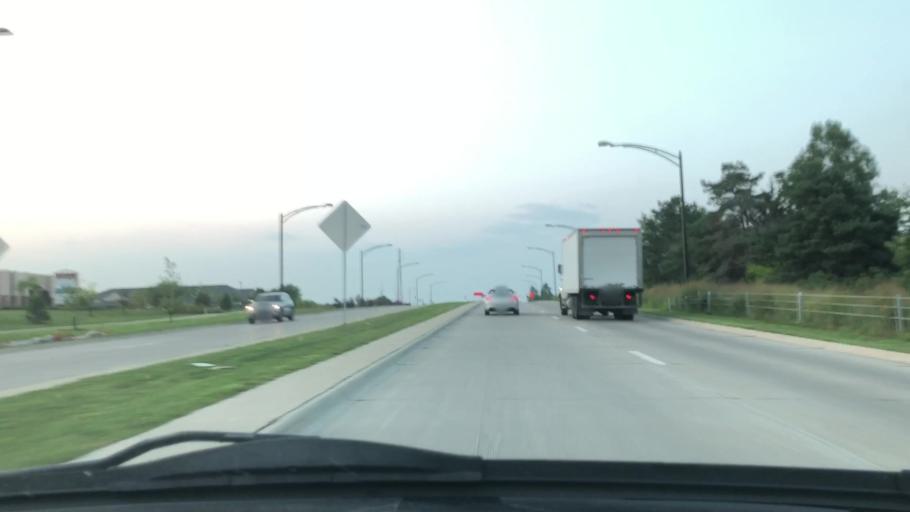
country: US
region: Iowa
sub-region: Johnson County
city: Coralville
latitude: 41.7052
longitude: -91.6081
